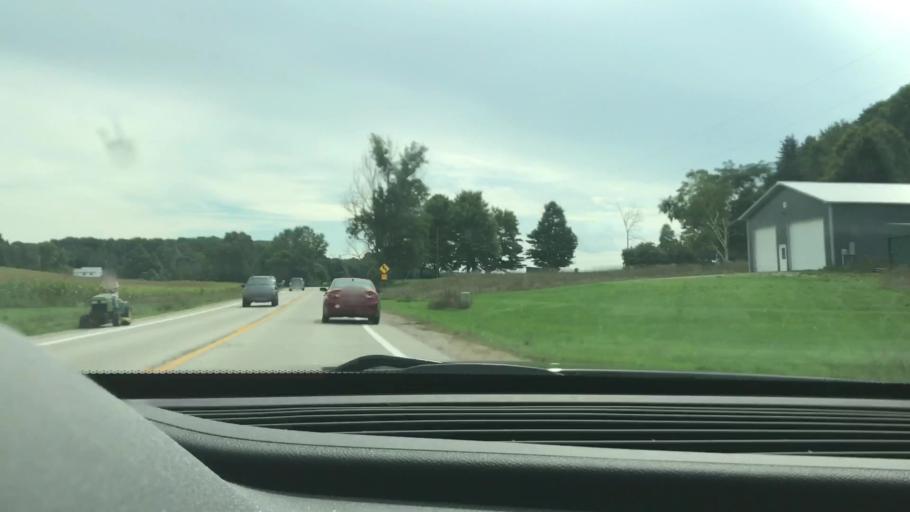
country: US
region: Michigan
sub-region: Antrim County
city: Bellaire
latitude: 45.0887
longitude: -85.2899
